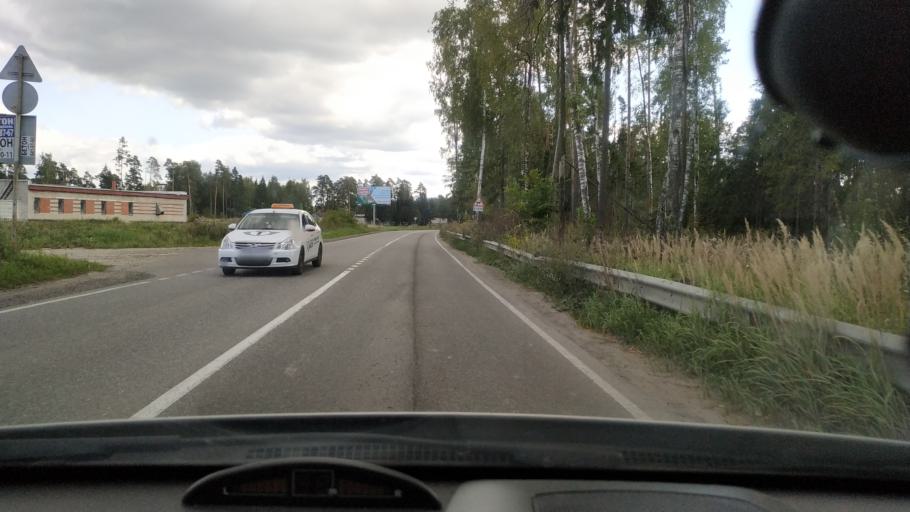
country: RU
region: Moskovskaya
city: Zheleznodorozhnyy
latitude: 55.7942
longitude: 38.0328
